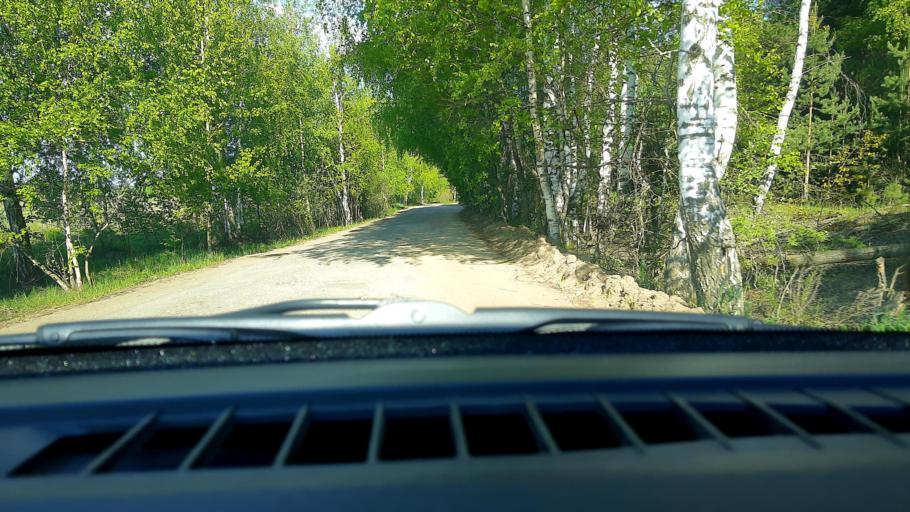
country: RU
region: Nizjnij Novgorod
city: Sitniki
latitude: 56.4135
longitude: 44.0592
